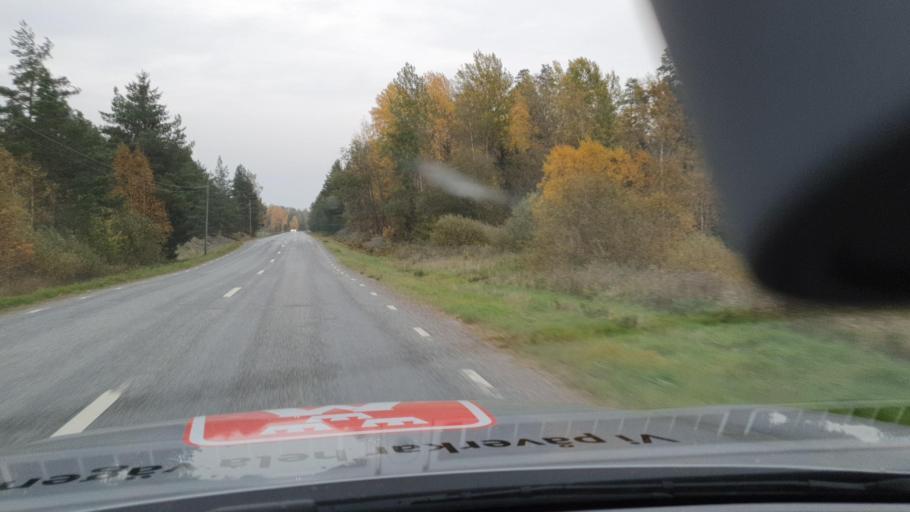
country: SE
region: Stockholm
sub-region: Sodertalje Kommun
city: Soedertaelje
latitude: 59.1479
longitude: 17.5349
